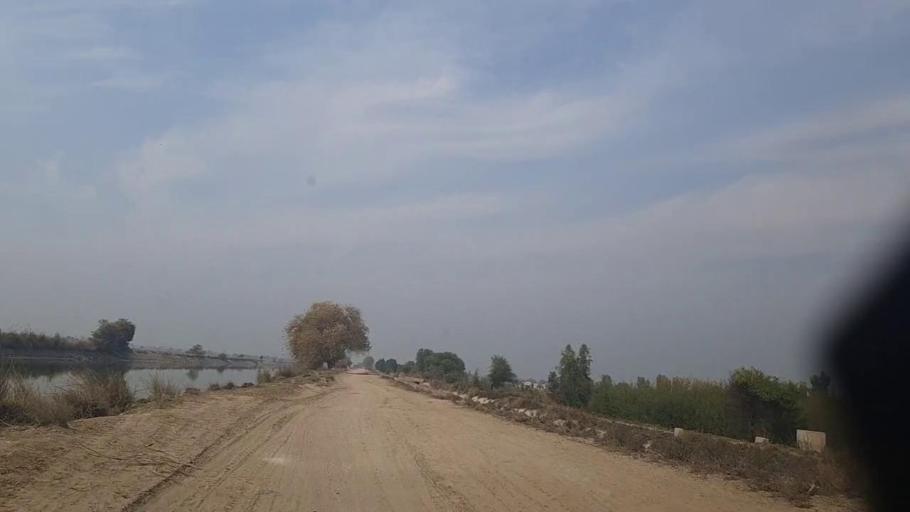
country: PK
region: Sindh
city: Daur
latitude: 26.3264
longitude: 68.1938
